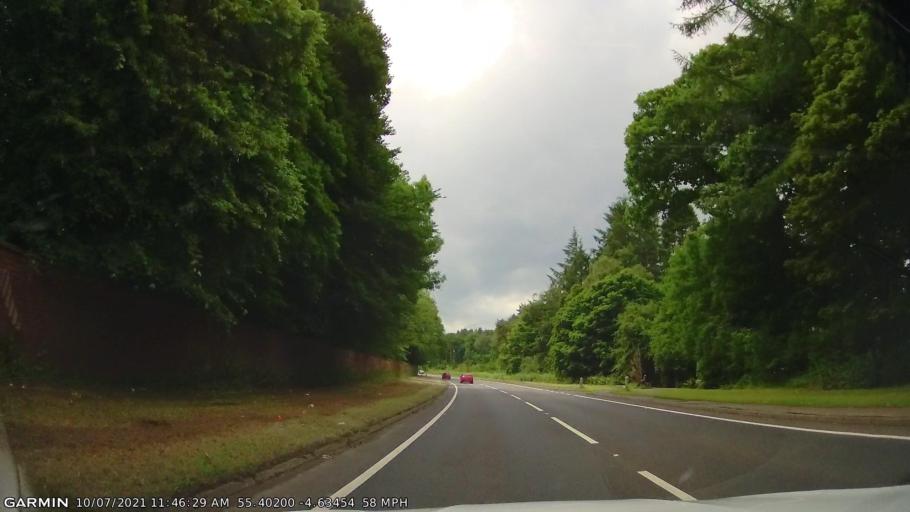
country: GB
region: Scotland
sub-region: East Ayrshire
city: Dalrymple
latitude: 55.4020
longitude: -4.6346
